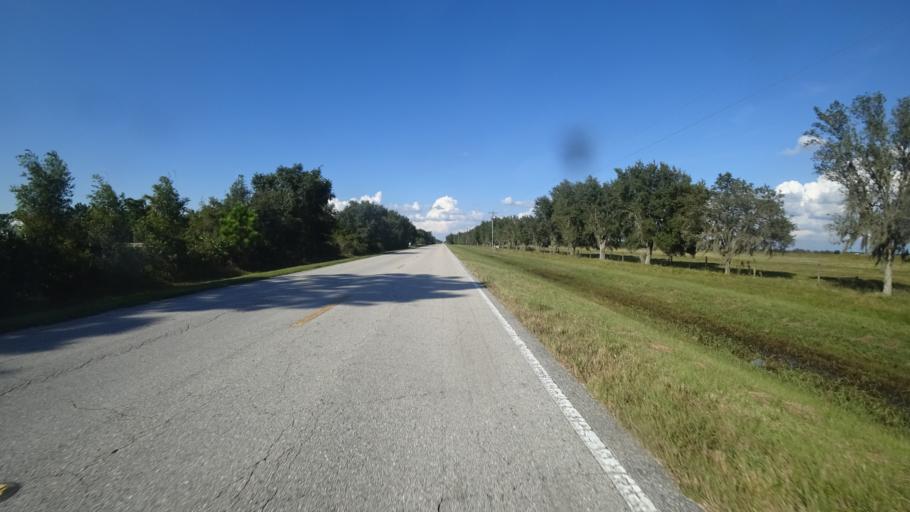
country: US
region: Florida
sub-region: Sarasota County
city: The Meadows
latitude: 27.4180
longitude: -82.3037
